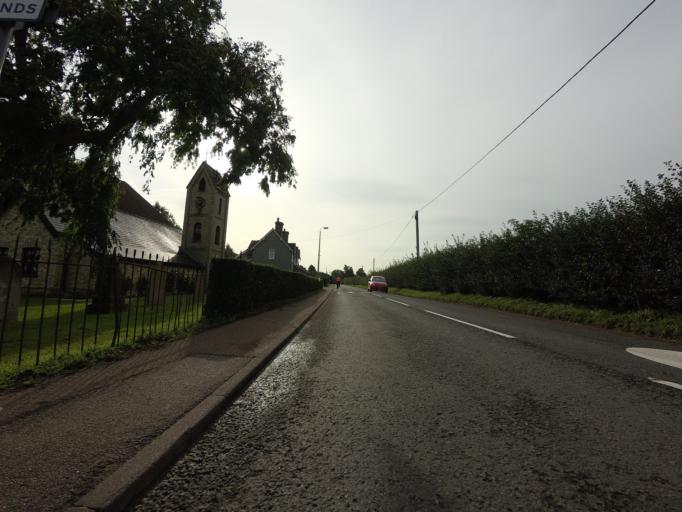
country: GB
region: England
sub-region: Cambridgeshire
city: Harston
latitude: 52.0903
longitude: 0.0731
